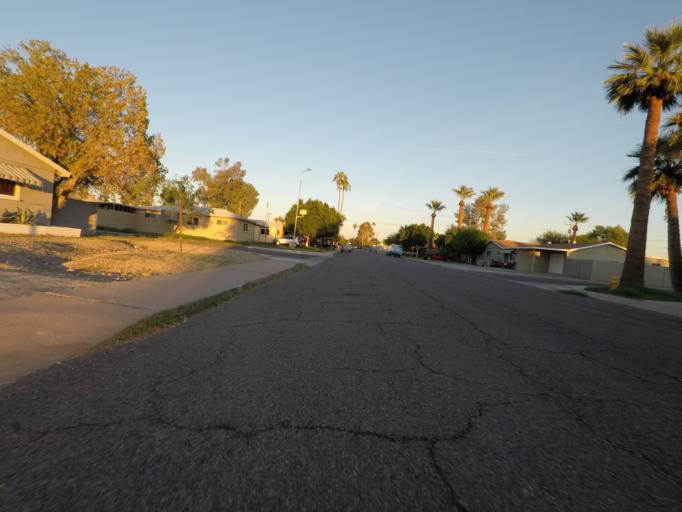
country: US
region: Arizona
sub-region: Maricopa County
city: Phoenix
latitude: 33.4764
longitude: -112.0014
